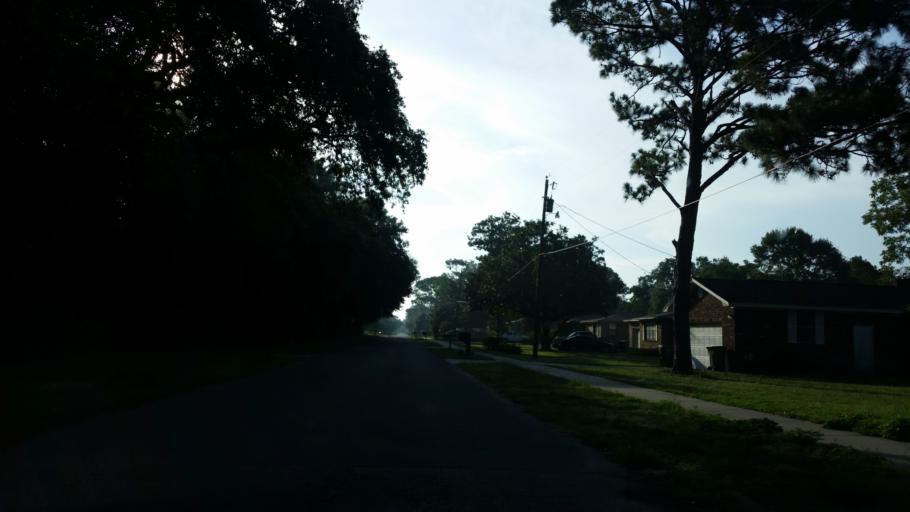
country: US
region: Florida
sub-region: Escambia County
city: Ferry Pass
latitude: 30.4901
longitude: -87.2077
